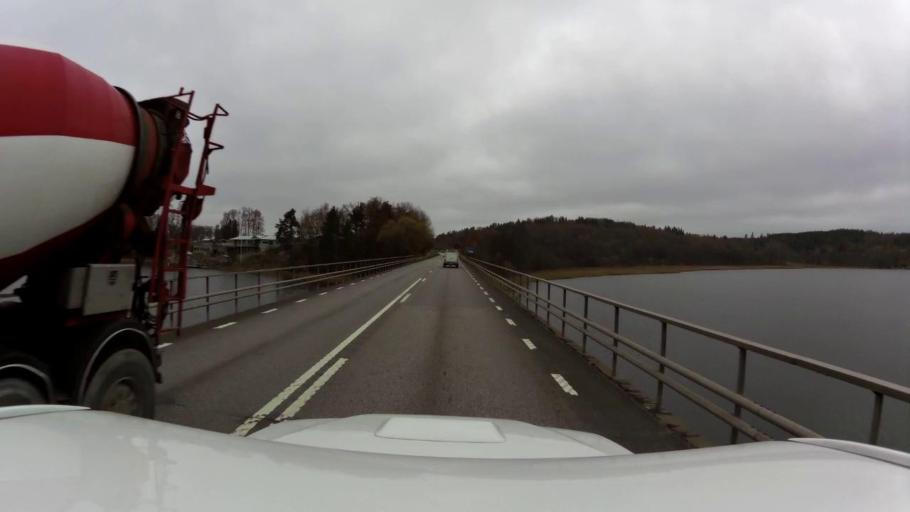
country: SE
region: OEstergoetland
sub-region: Kinda Kommun
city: Rimforsa
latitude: 58.1688
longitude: 15.6775
